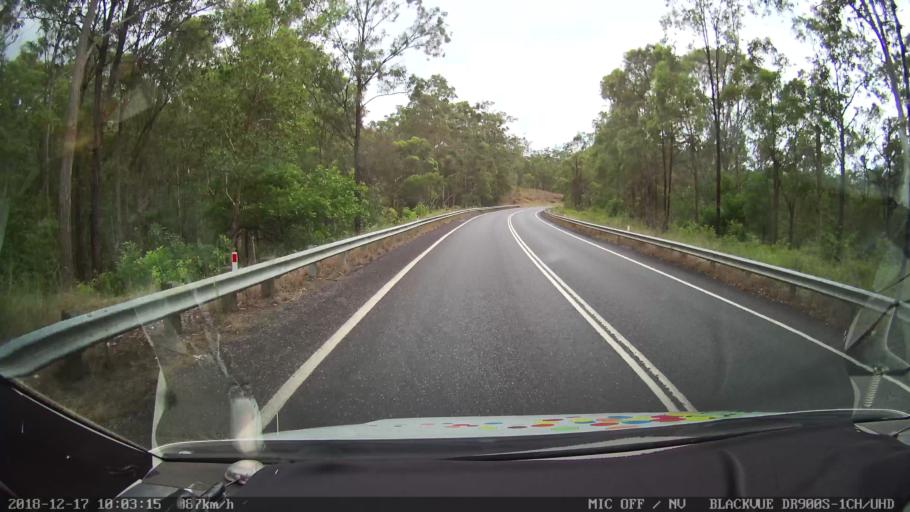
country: AU
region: New South Wales
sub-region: Tenterfield Municipality
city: Carrolls Creek
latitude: -28.8982
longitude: 152.4613
